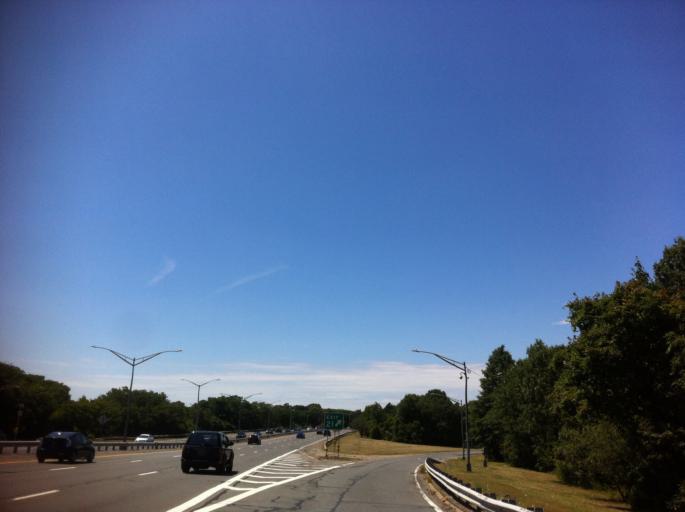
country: US
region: New York
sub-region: Nassau County
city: Bellerose Terrace
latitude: 40.7432
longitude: -73.7332
